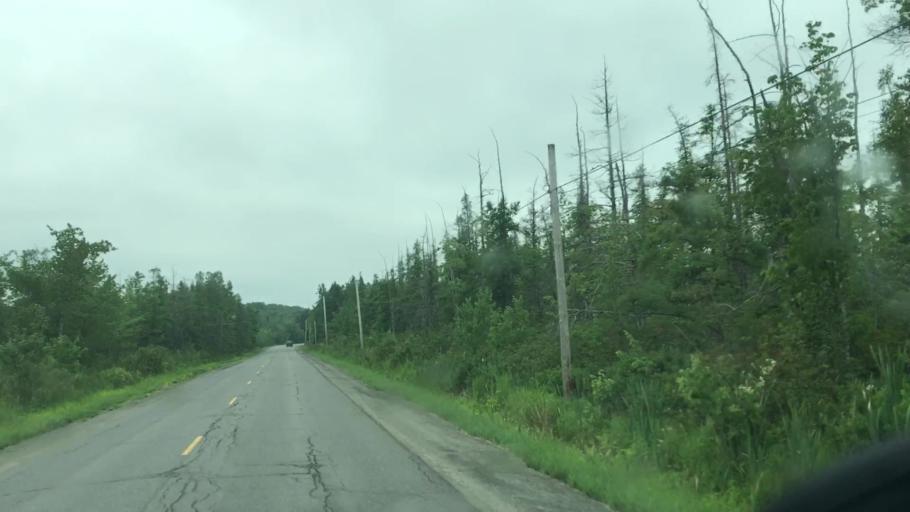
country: US
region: Maine
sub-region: Penobscot County
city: Veazie
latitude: 44.8700
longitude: -68.7155
